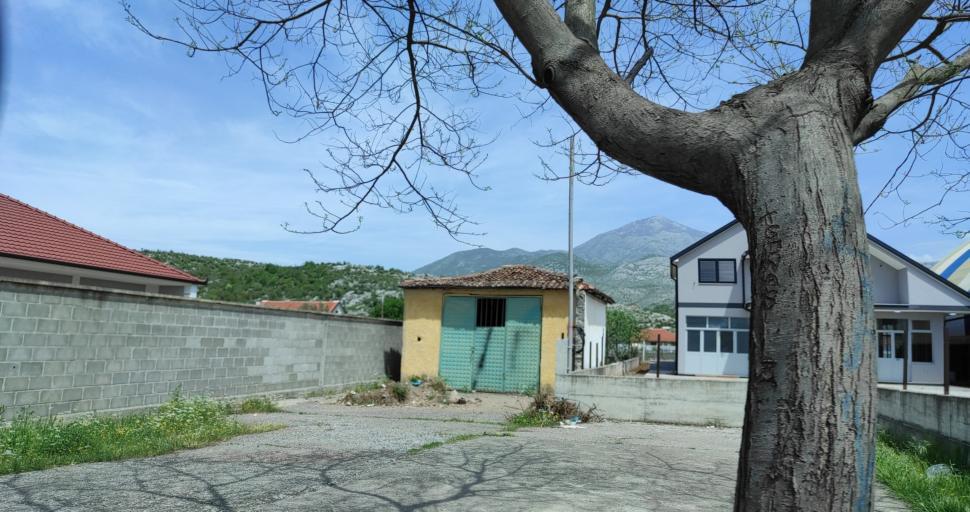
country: AL
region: Shkoder
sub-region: Rrethi i Malesia e Madhe
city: Gruemire
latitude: 42.1205
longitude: 19.5654
